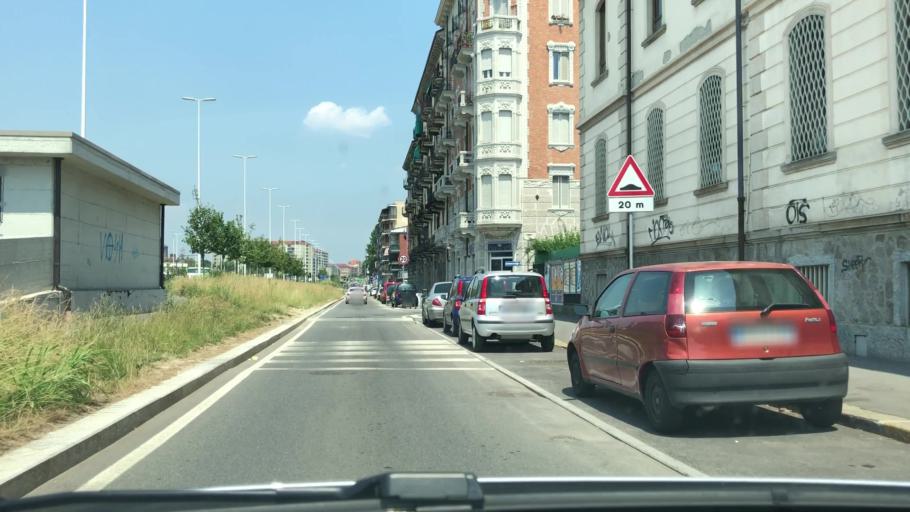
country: IT
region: Piedmont
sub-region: Provincia di Torino
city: Turin
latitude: 45.0847
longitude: 7.6743
